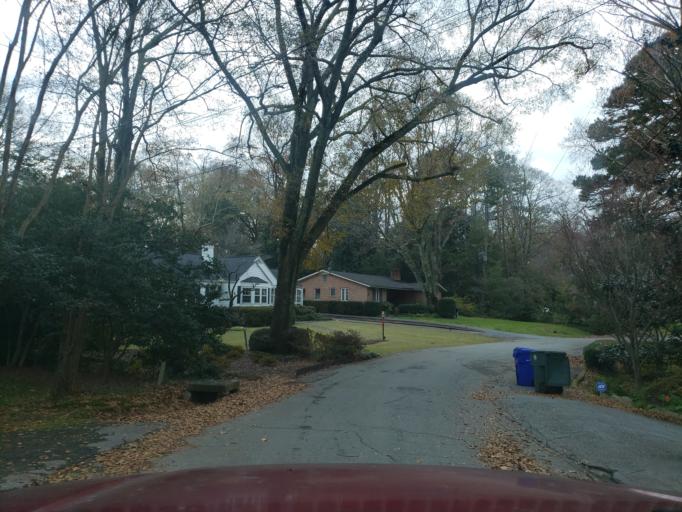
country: US
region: South Carolina
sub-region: Greenville County
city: Greenville
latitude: 34.8157
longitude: -82.3803
